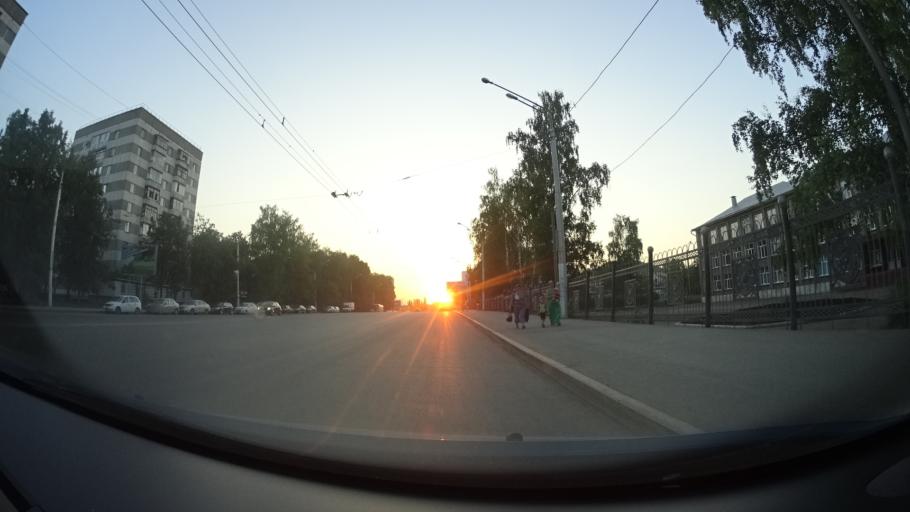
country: RU
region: Bashkortostan
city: Ufa
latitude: 54.7480
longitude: 55.9899
